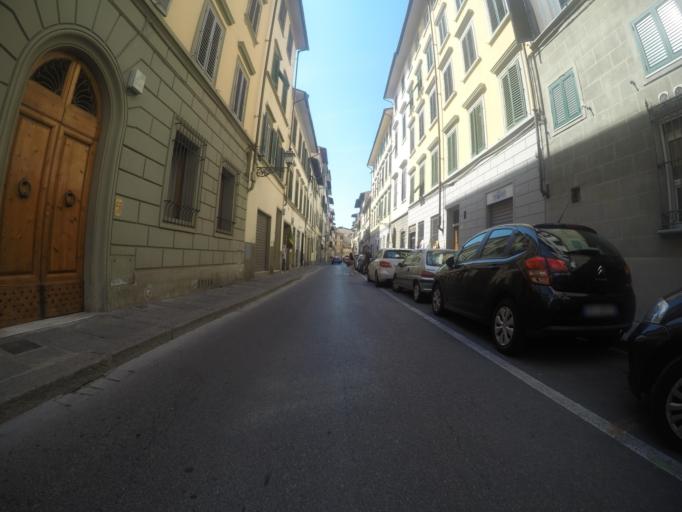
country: IT
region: Tuscany
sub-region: Province of Florence
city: Florence
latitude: 43.7791
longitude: 11.2553
